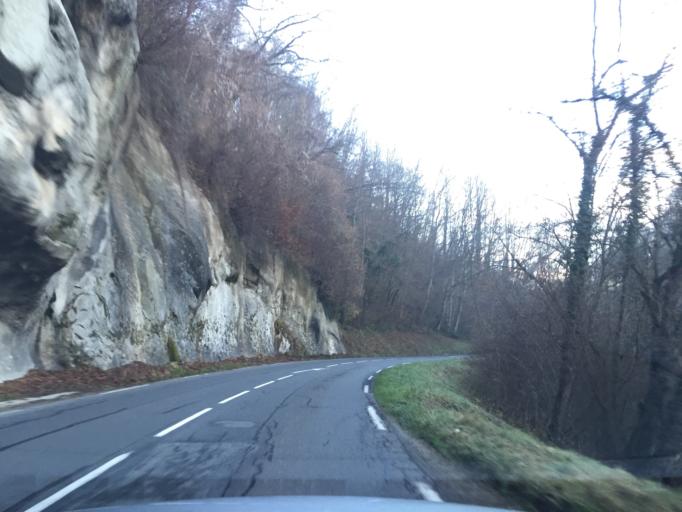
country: FR
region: Rhone-Alpes
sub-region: Departement de la Savoie
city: Gresy-sur-Aix
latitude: 45.7289
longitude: 5.9484
